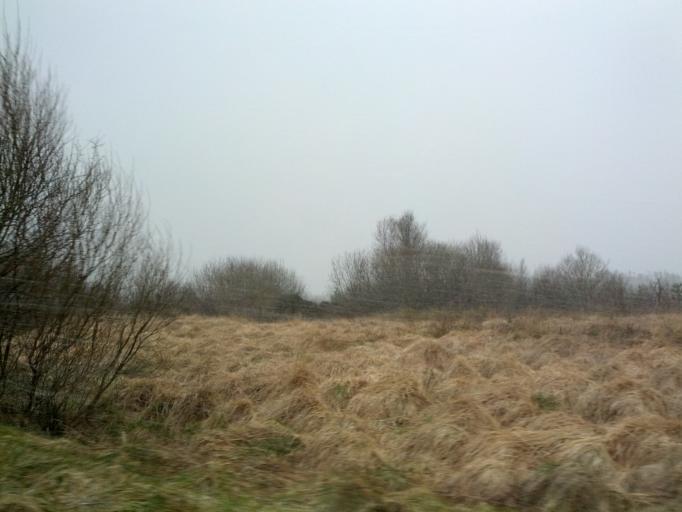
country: IE
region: Connaught
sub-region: County Galway
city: Athenry
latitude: 53.4056
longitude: -8.5939
